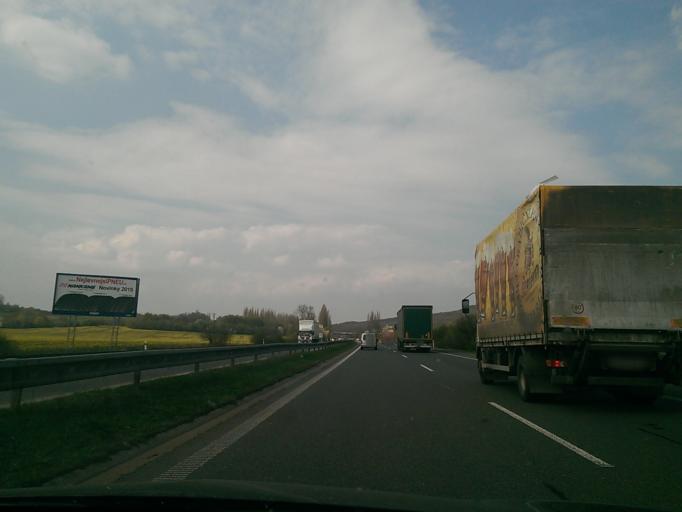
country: CZ
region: Central Bohemia
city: Kosmonosy
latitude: 50.4352
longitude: 14.9434
